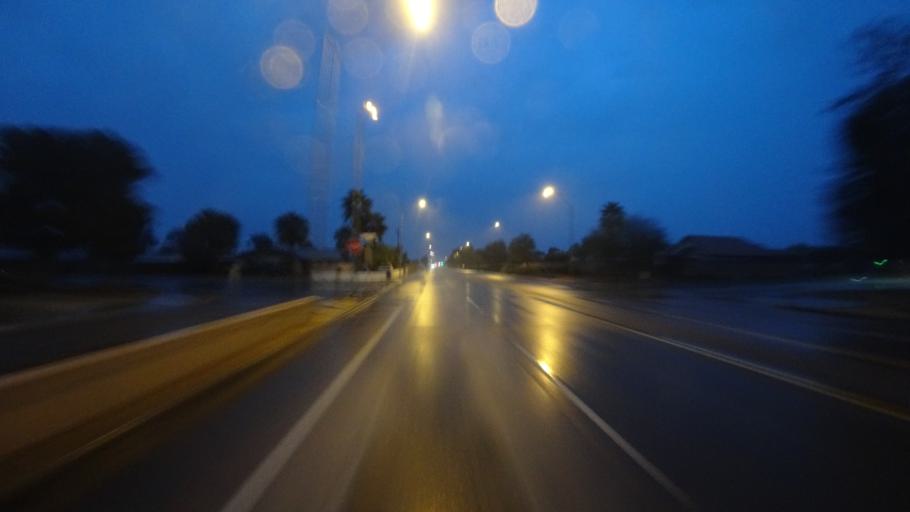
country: US
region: Arizona
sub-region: Maricopa County
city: Paradise Valley
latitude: 33.6551
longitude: -111.9902
